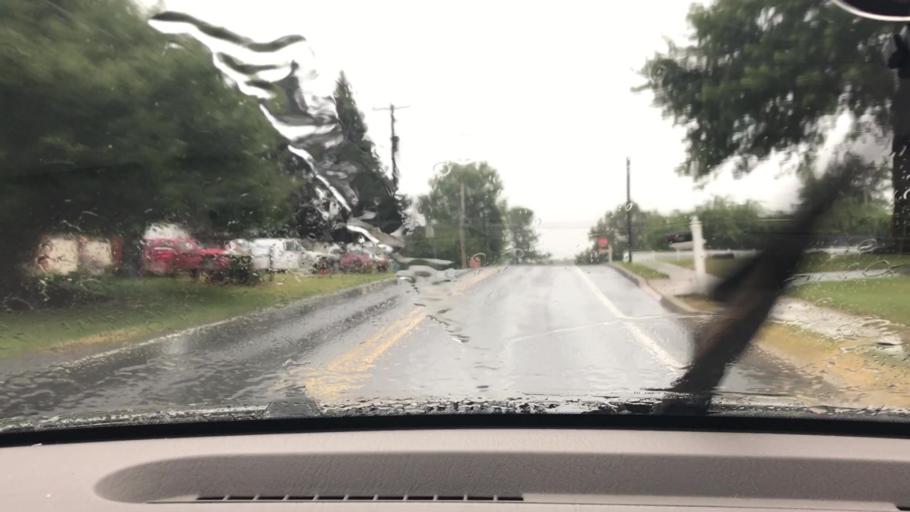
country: US
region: Pennsylvania
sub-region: Lancaster County
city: Elizabethtown
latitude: 40.1288
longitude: -76.6124
